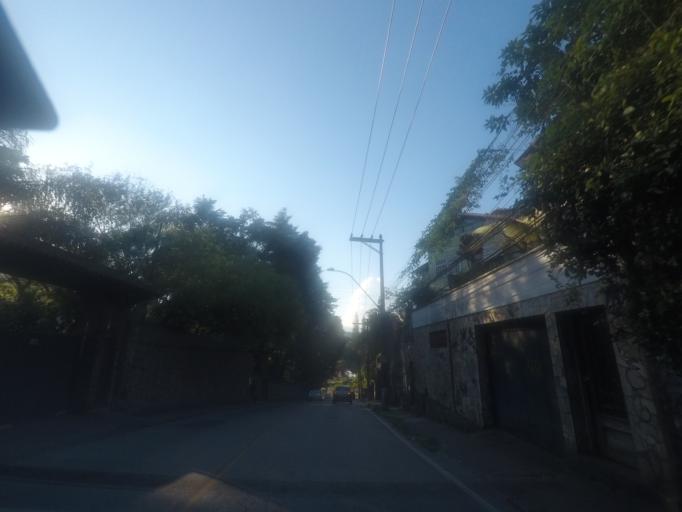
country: BR
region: Rio de Janeiro
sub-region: Petropolis
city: Petropolis
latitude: -22.5269
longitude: -43.1795
